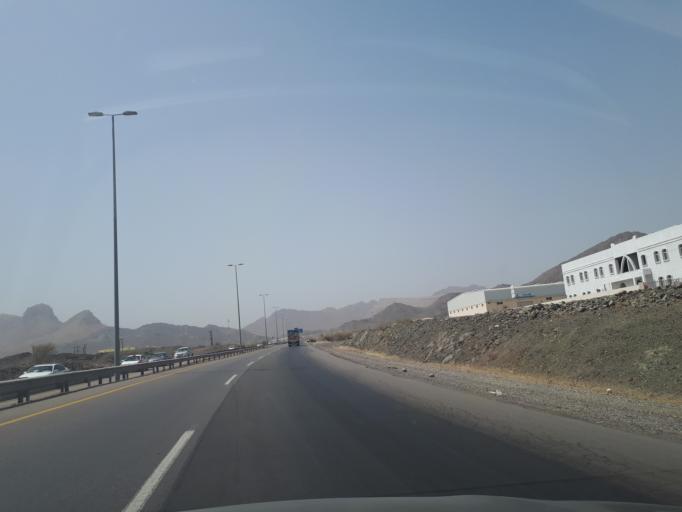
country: OM
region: Muhafazat ad Dakhiliyah
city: Bidbid
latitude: 23.4975
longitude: 58.1961
